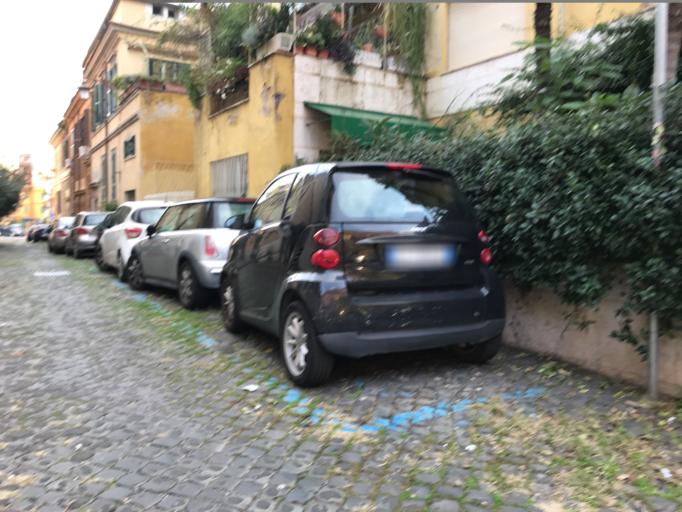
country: IT
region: Latium
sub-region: Citta metropolitana di Roma Capitale
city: Rome
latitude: 41.9093
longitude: 12.5147
